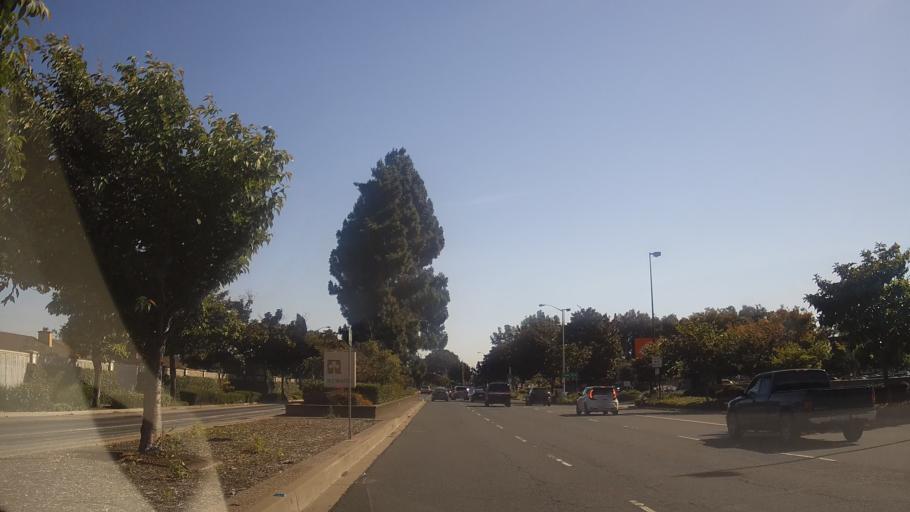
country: US
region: California
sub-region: Alameda County
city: Newark
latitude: 37.5443
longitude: -122.0248
